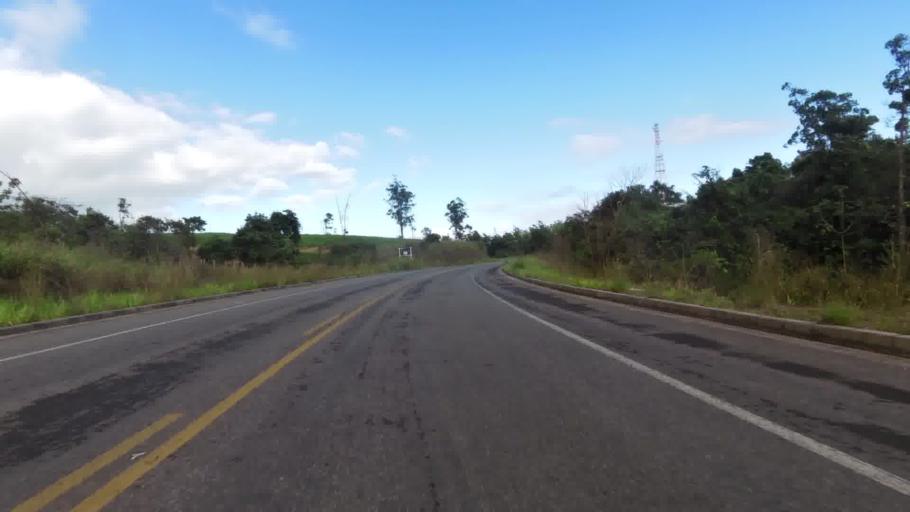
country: BR
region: Espirito Santo
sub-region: Piuma
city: Piuma
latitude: -20.7944
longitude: -40.6112
